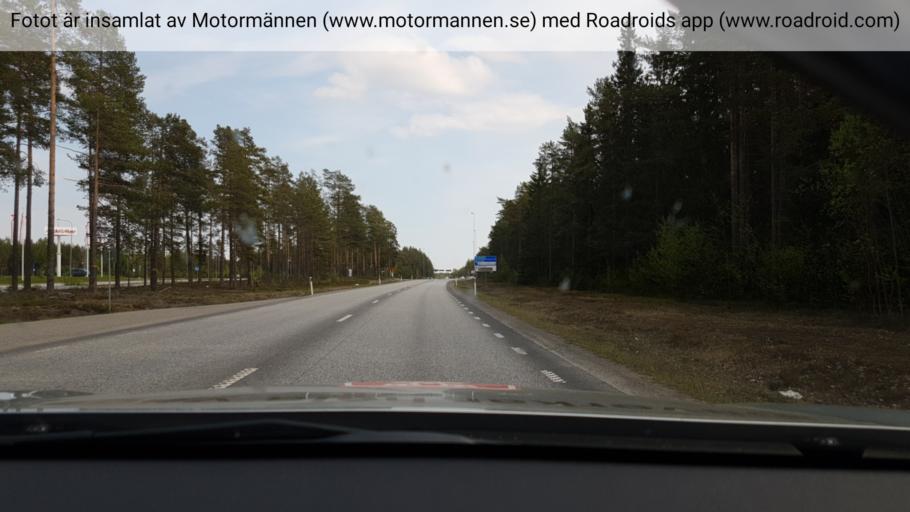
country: SE
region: Vaesterbotten
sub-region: Umea Kommun
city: Roback
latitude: 63.8470
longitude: 20.1527
